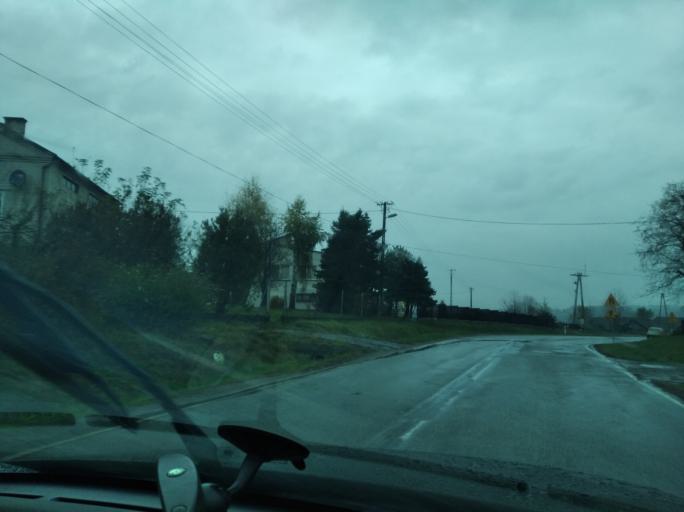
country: PL
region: Subcarpathian Voivodeship
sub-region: Powiat lancucki
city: Albigowa
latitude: 50.0101
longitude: 22.2188
